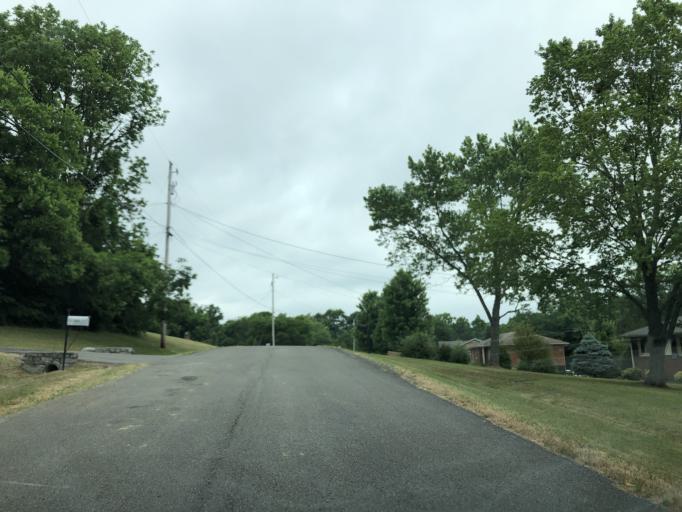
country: US
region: Tennessee
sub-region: Davidson County
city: Goodlettsville
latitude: 36.2836
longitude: -86.7380
